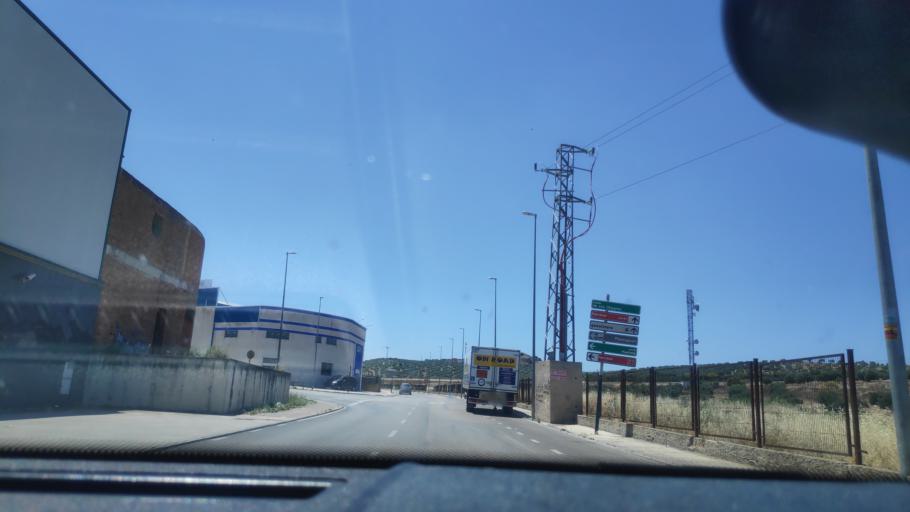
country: ES
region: Andalusia
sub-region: Provincia de Jaen
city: Jaen
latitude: 37.8039
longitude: -3.7837
